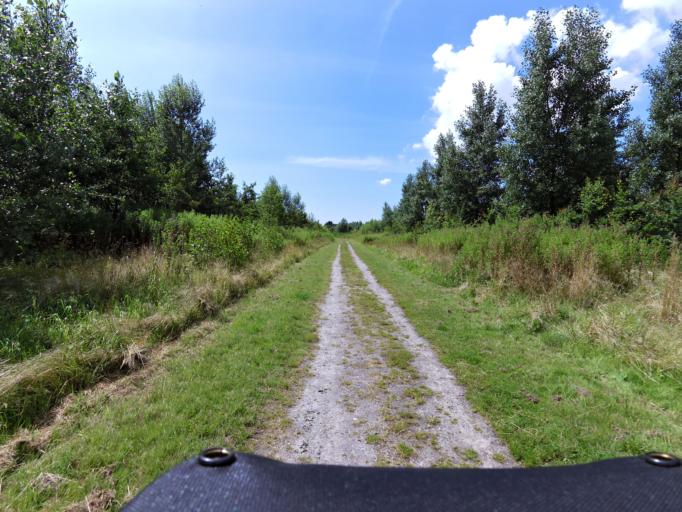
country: NL
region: South Holland
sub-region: Gemeente Albrandswaard
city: Rhoon
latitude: 51.8664
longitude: 4.4288
